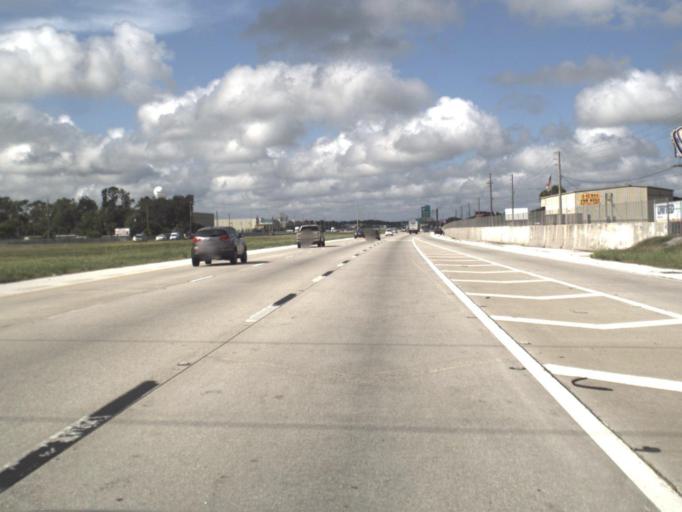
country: US
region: Florida
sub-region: Polk County
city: Winston
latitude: 28.0483
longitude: -82.0205
